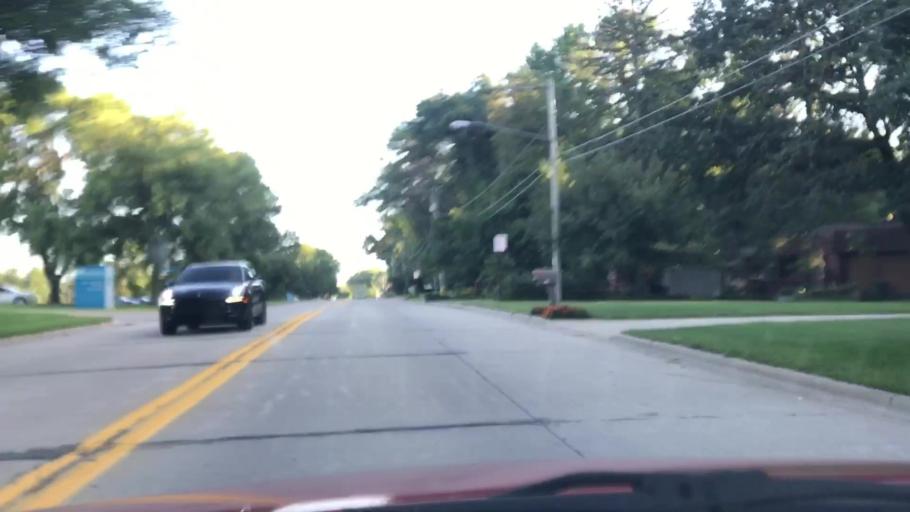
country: US
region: Wisconsin
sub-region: Brown County
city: Howard
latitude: 44.5274
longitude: -88.1096
